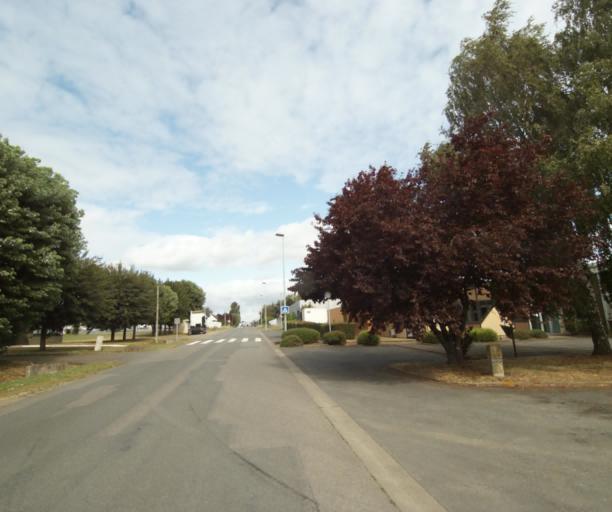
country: FR
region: Pays de la Loire
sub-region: Departement de la Sarthe
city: Solesmes
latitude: 47.8212
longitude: -0.3051
